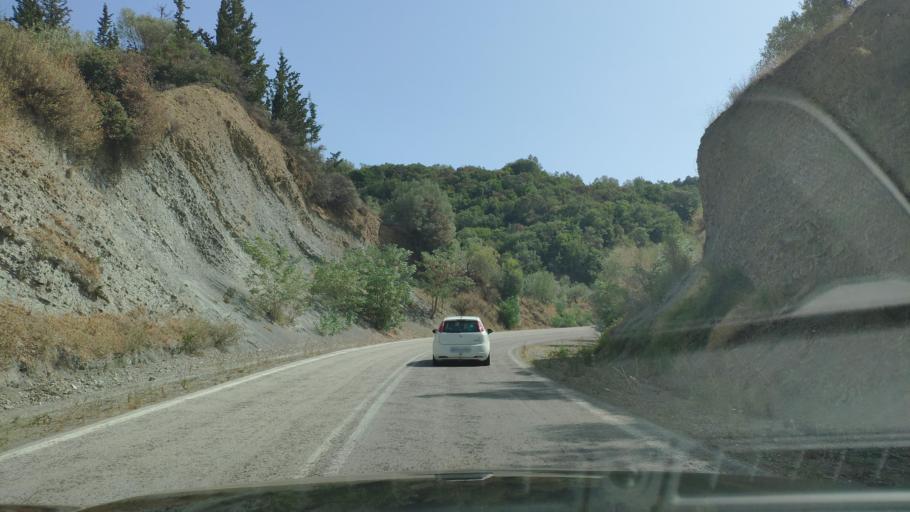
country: GR
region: Epirus
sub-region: Nomos Artas
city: Peta
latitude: 39.1690
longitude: 21.0411
